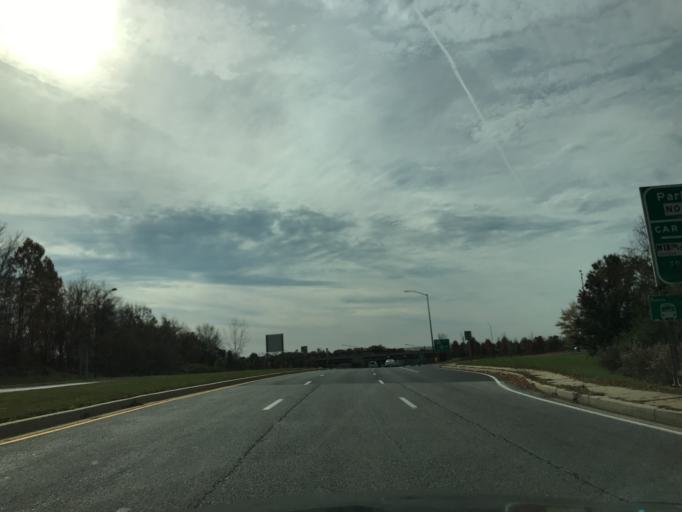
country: US
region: Maryland
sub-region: Howard County
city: Columbia
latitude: 39.1935
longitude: -76.8098
